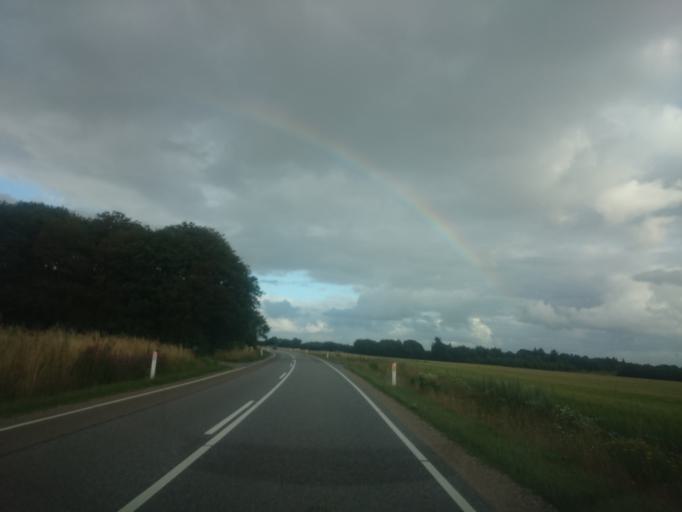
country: DK
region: South Denmark
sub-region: Billund Kommune
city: Grindsted
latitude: 55.6596
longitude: 8.7809
